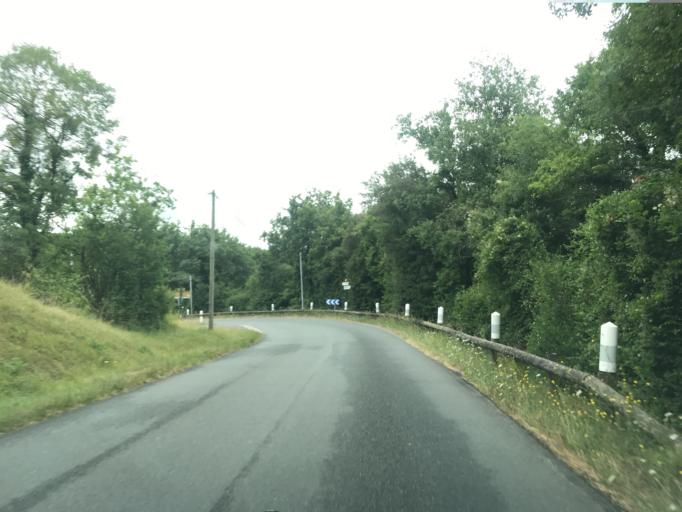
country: FR
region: Poitou-Charentes
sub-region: Departement de la Charente
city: Puymoyen
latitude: 45.6012
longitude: 0.1963
